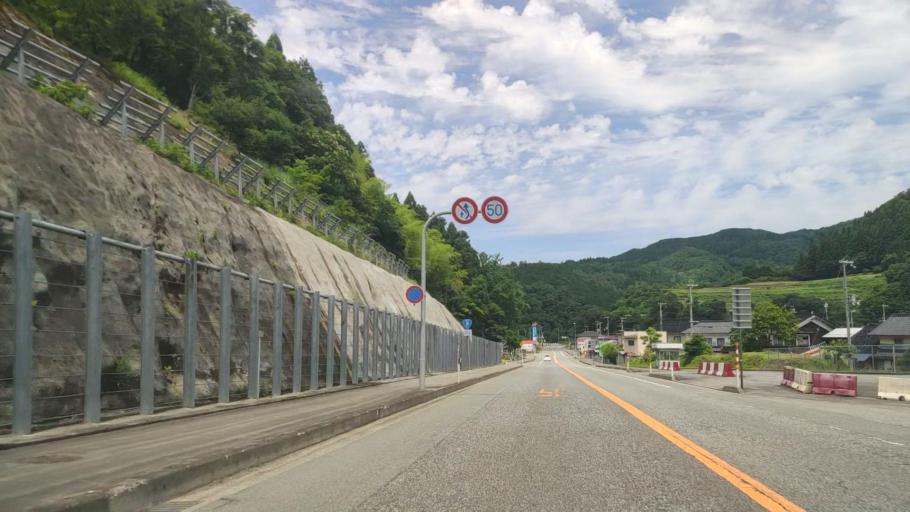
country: JP
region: Hyogo
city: Toyooka
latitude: 35.4742
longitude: 134.5881
